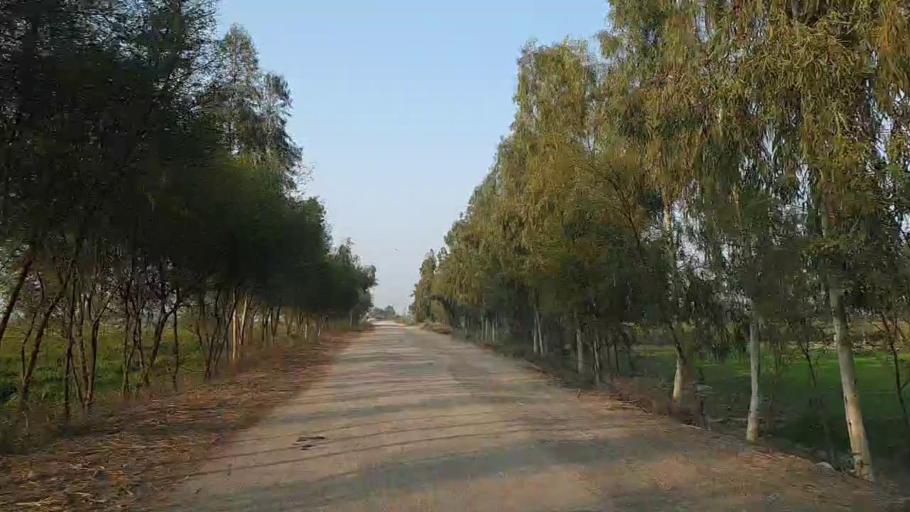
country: PK
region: Sindh
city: Daur
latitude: 26.4213
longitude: 68.3935
